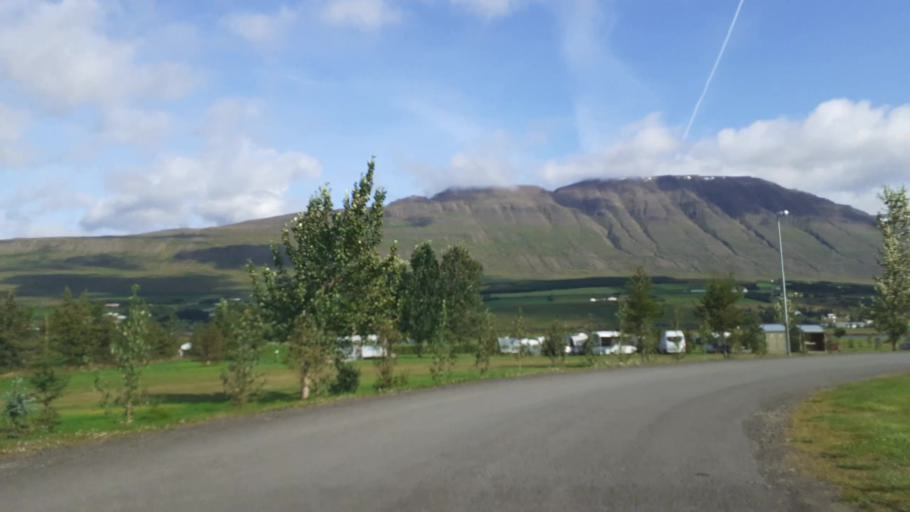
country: IS
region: Northeast
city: Akureyri
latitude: 65.5742
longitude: -18.0923
